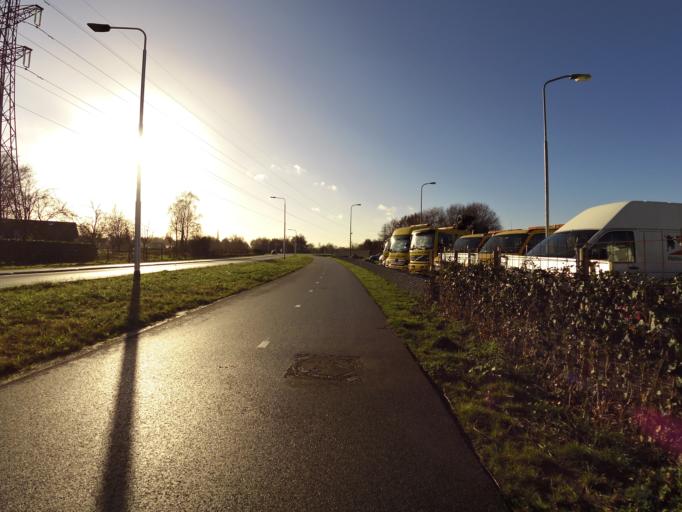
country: NL
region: Gelderland
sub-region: Gemeente Zevenaar
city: Zevenaar
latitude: 51.9320
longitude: 6.1408
